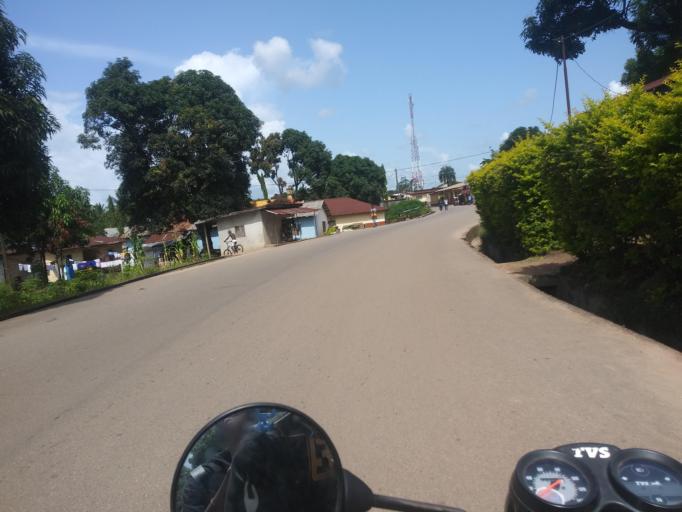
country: SL
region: Northern Province
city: Makeni
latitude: 8.8763
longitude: -12.0357
